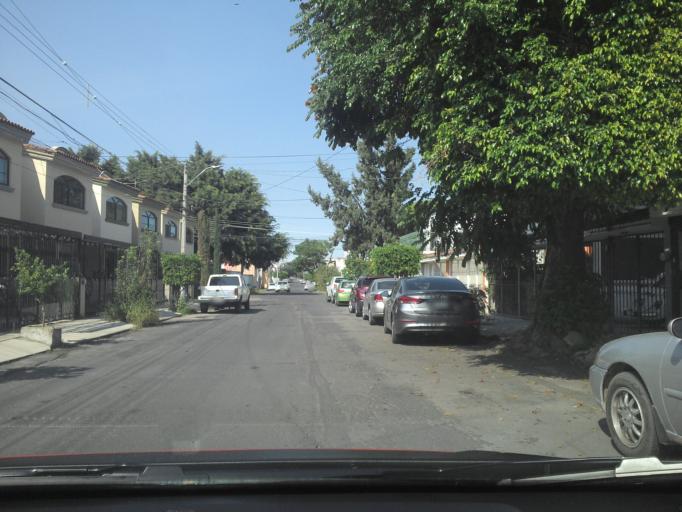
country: MX
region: Jalisco
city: Guadalajara
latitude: 20.6427
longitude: -103.4341
